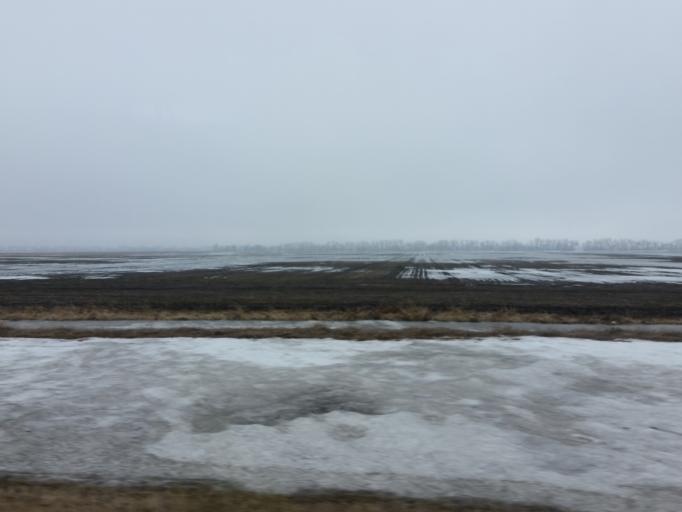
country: US
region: North Dakota
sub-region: Walsh County
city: Grafton
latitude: 48.5718
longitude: -97.3366
